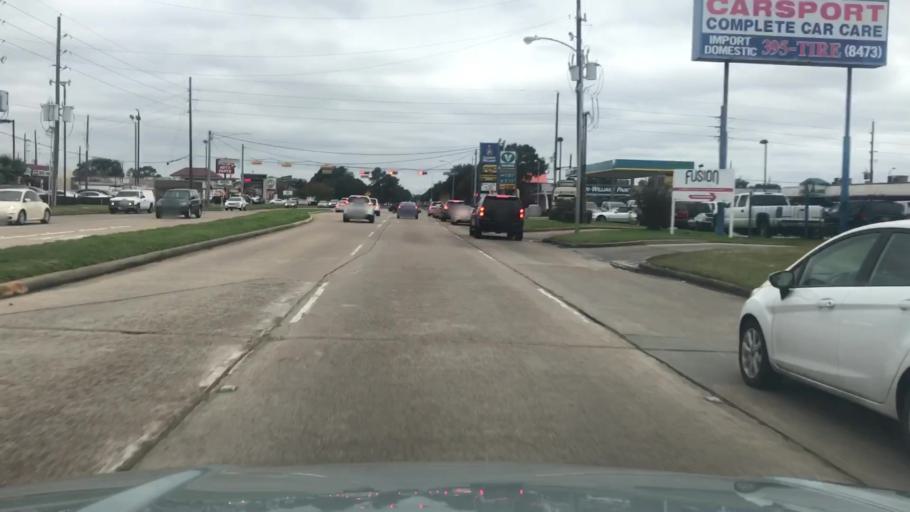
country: US
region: Texas
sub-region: Fort Bend County
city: Cinco Ranch
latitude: 29.7655
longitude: -95.7517
